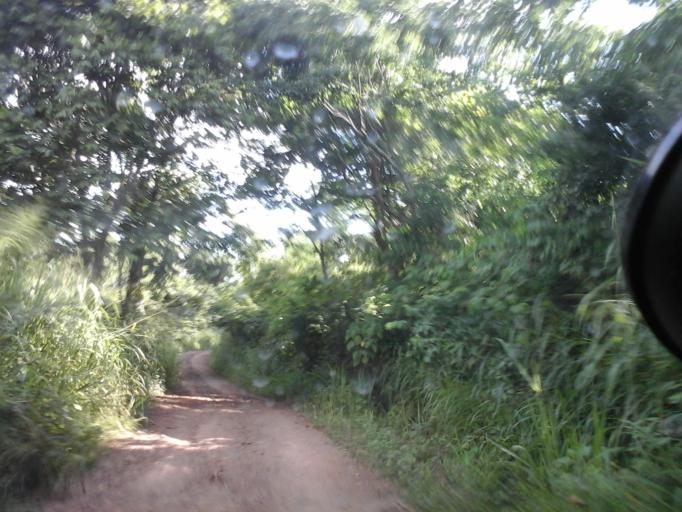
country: CO
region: Cesar
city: San Diego
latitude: 10.2707
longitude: -73.0955
